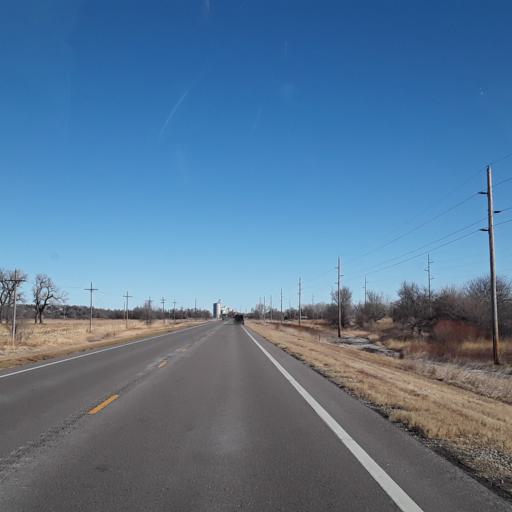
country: US
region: Kansas
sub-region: Pawnee County
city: Larned
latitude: 38.1622
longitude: -99.1183
